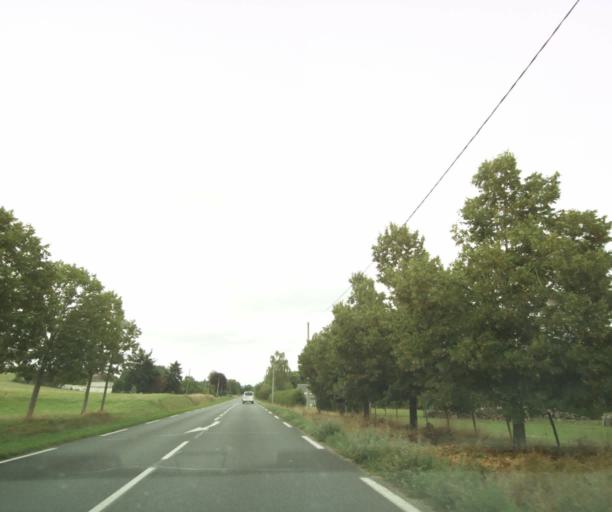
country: FR
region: Centre
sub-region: Departement d'Indre-et-Loire
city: Perrusson
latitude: 47.0614
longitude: 1.0826
